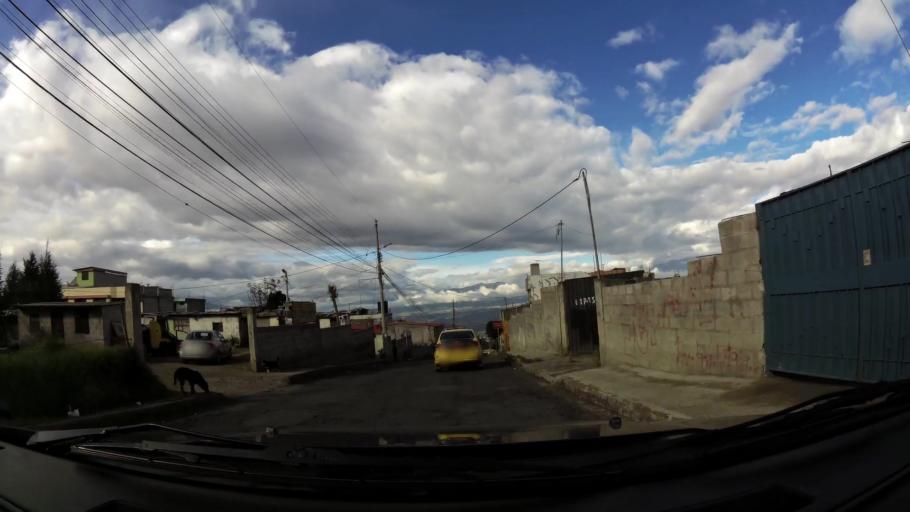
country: EC
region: Pichincha
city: Quito
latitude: -0.1340
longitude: -78.4574
